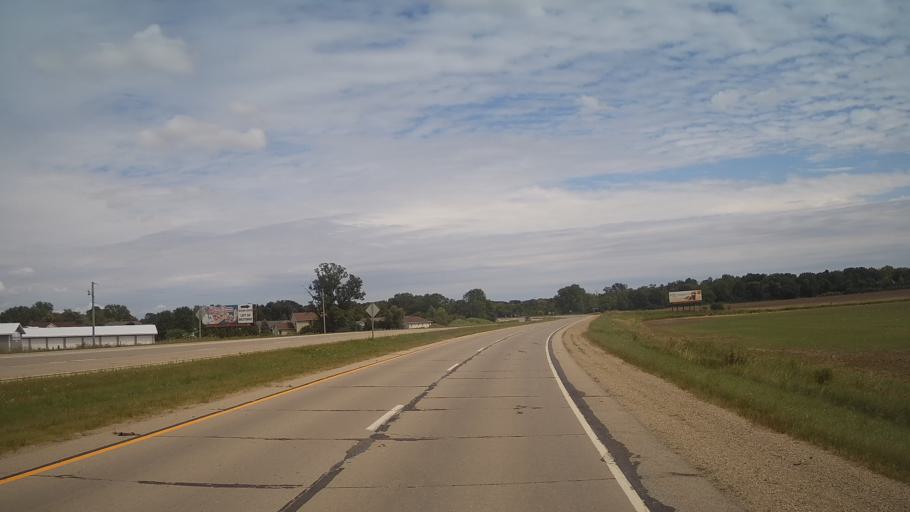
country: US
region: Wisconsin
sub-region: Winnebago County
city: Oshkosh
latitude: 44.0318
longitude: -88.6211
